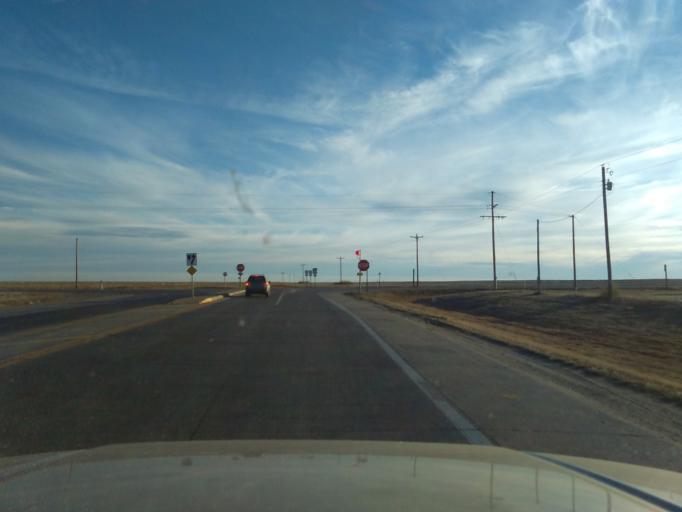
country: US
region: Kansas
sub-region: Logan County
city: Oakley
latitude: 39.1201
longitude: -100.8682
